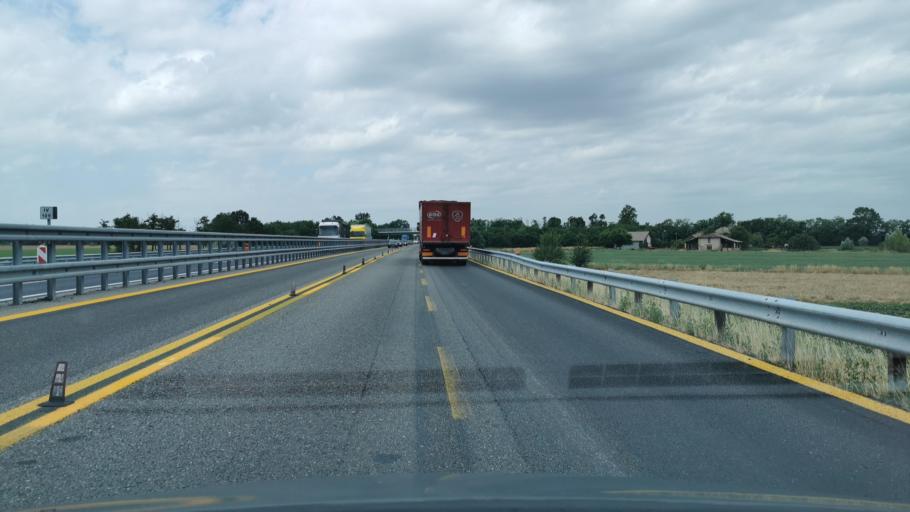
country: IT
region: Lombardy
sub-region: Provincia di Pavia
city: Lungavilla
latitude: 45.0253
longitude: 9.0675
